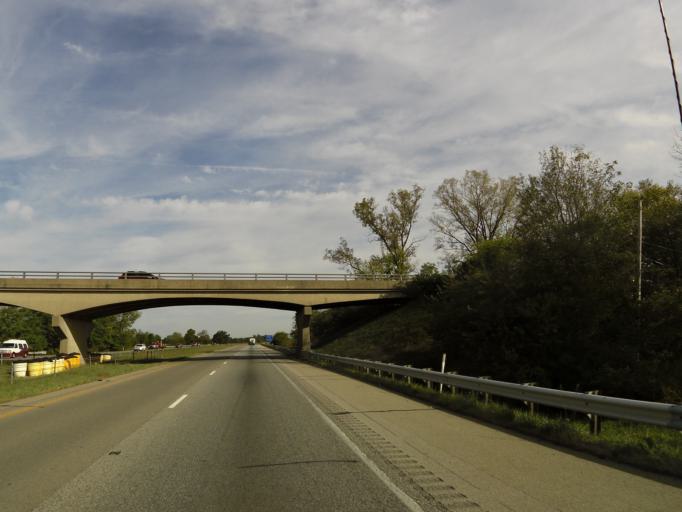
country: US
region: Indiana
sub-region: Bartholomew County
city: Lowell
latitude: 39.2438
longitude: -85.9545
